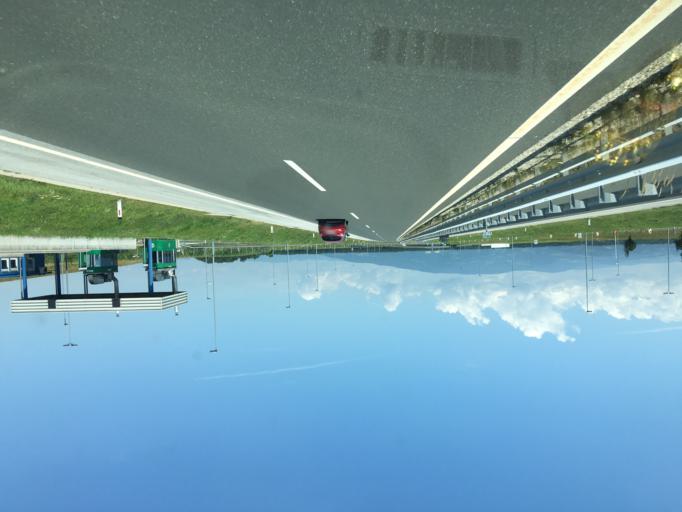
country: SI
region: Starse
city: Starse
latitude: 46.4523
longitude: 15.7596
